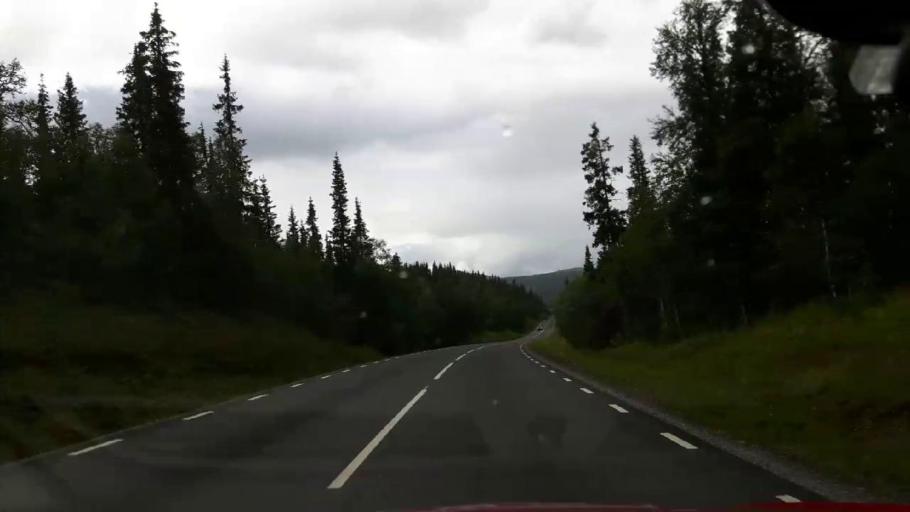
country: NO
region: Nord-Trondelag
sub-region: Royrvik
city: Royrvik
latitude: 64.9081
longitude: 14.2063
